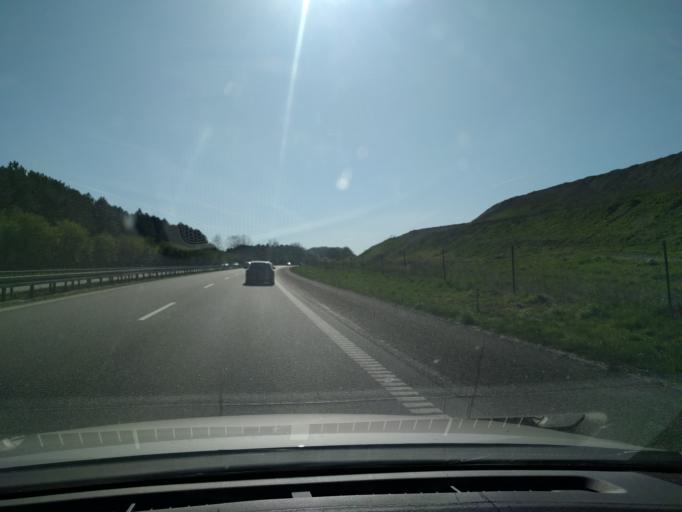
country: DK
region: Zealand
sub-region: Slagelse Kommune
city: Slagelse
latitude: 55.4104
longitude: 11.4047
